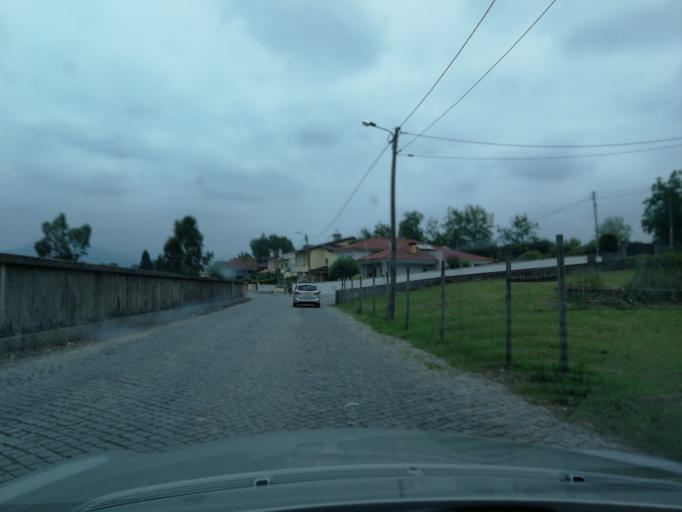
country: PT
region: Braga
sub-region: Vila Verde
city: Prado
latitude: 41.6014
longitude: -8.4378
